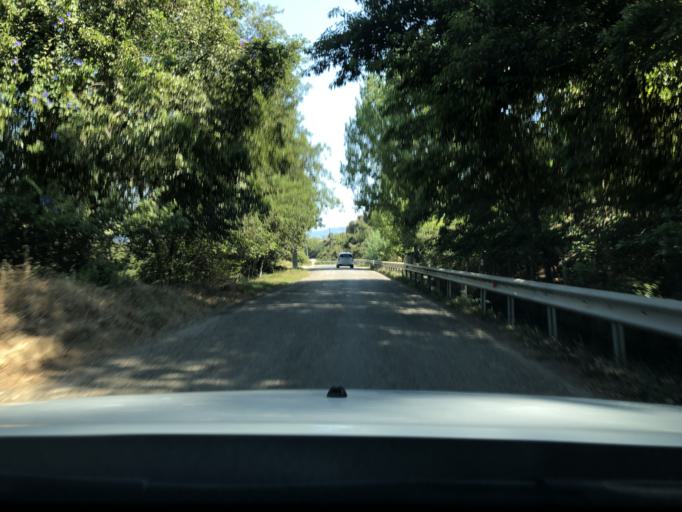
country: TR
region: Antalya
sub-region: Manavgat
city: Manavgat
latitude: 36.7988
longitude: 31.4669
